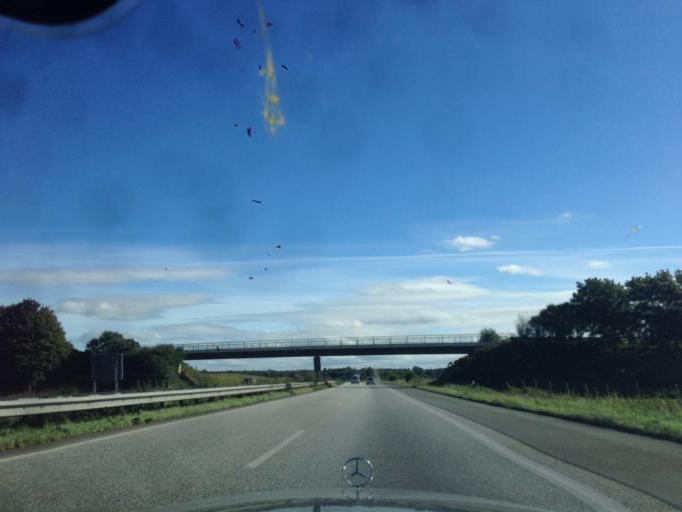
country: DE
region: Schleswig-Holstein
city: Schuby
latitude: 54.5353
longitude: 9.4750
